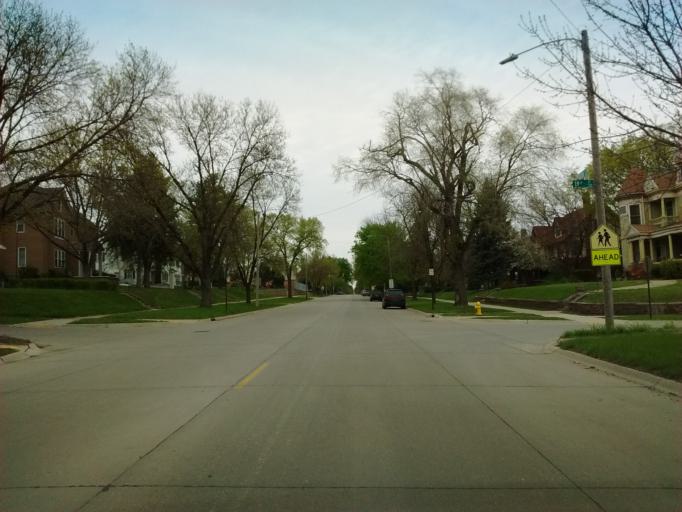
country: US
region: Iowa
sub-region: Woodbury County
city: Sioux City
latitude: 42.5098
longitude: -96.4020
